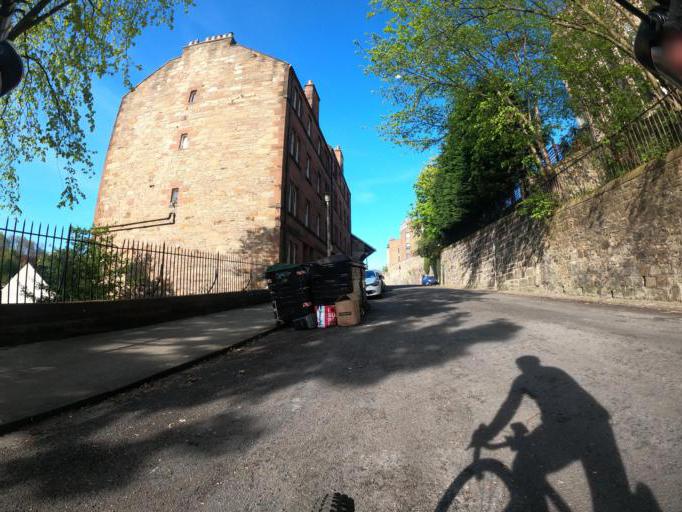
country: GB
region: Scotland
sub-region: Edinburgh
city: Edinburgh
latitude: 55.9516
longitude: -3.2168
